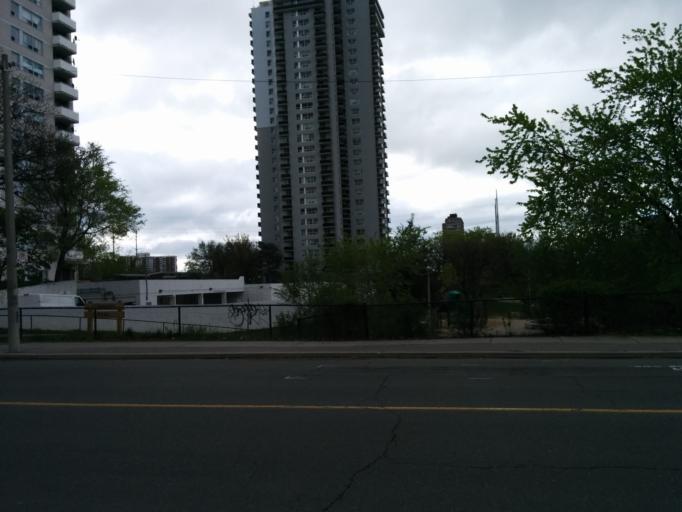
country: CA
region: Ontario
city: Willowdale
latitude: 43.7164
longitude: -79.3318
